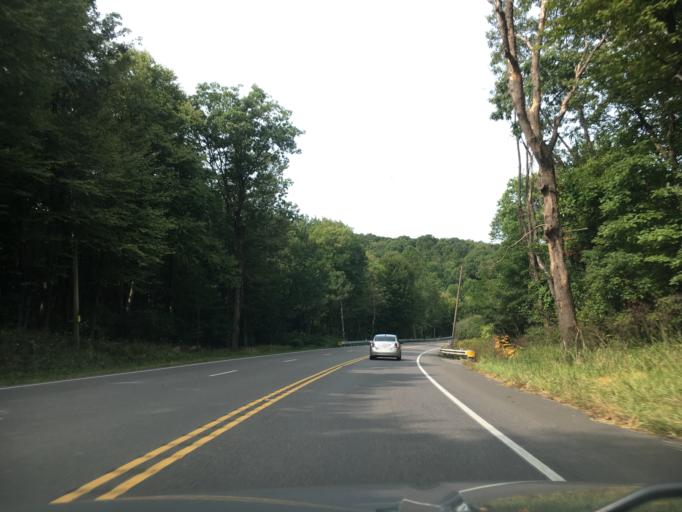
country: US
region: Pennsylvania
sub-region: Carbon County
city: Summit Hill
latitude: 40.7076
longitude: -75.8245
